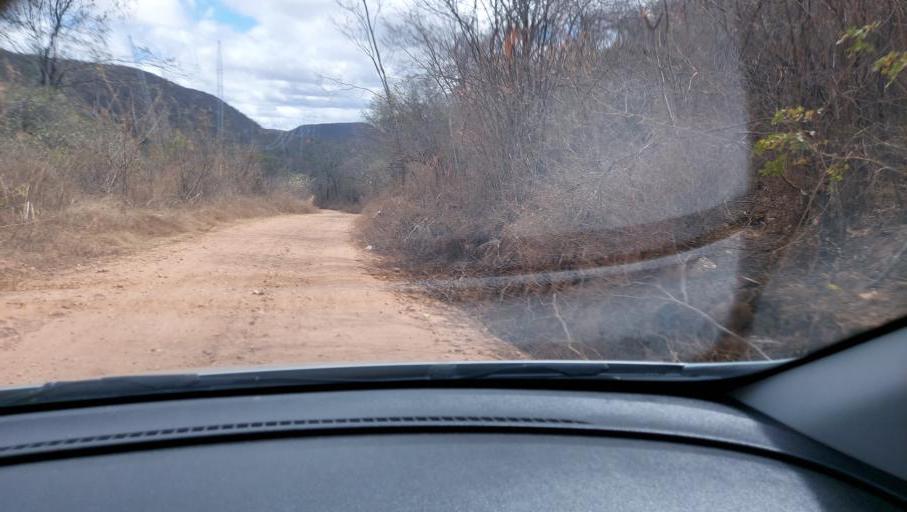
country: BR
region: Bahia
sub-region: Oliveira Dos Brejinhos
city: Beira Rio
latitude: -12.0834
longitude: -42.5433
